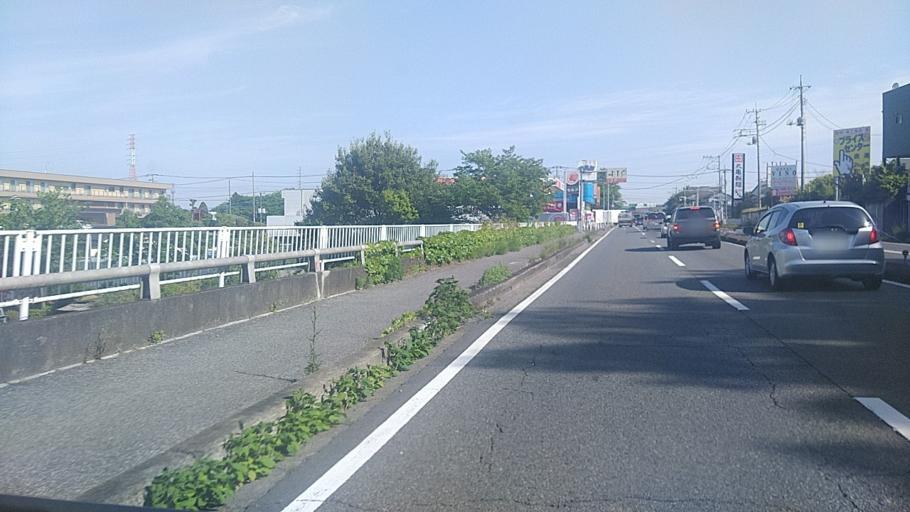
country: JP
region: Saitama
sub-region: Kawaguchi-shi
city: Hatogaya-honcho
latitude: 35.8447
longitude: 139.7343
